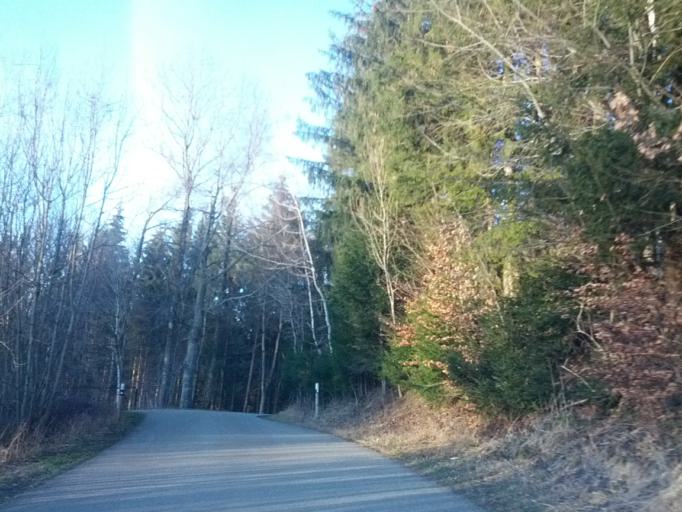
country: DE
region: Bavaria
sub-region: Swabia
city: Woringen
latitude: 47.8763
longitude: 10.1944
